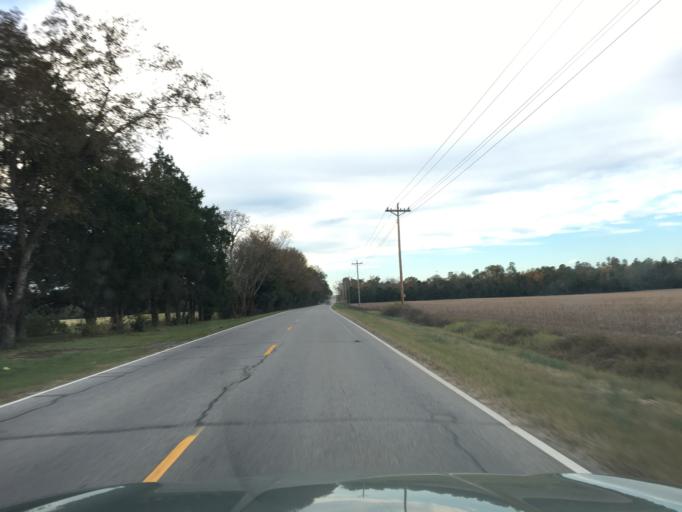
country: US
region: South Carolina
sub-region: Lexington County
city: Leesville
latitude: 33.7656
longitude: -81.3820
